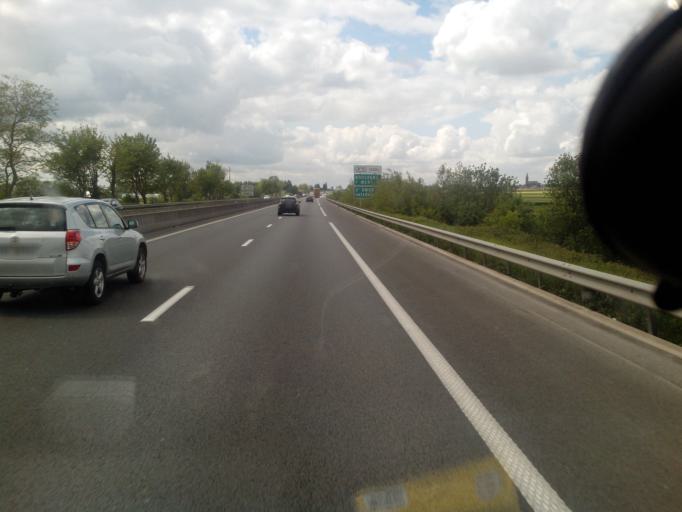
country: FR
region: Nord-Pas-de-Calais
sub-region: Departement du Nord
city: Meteren
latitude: 50.7284
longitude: 2.7143
